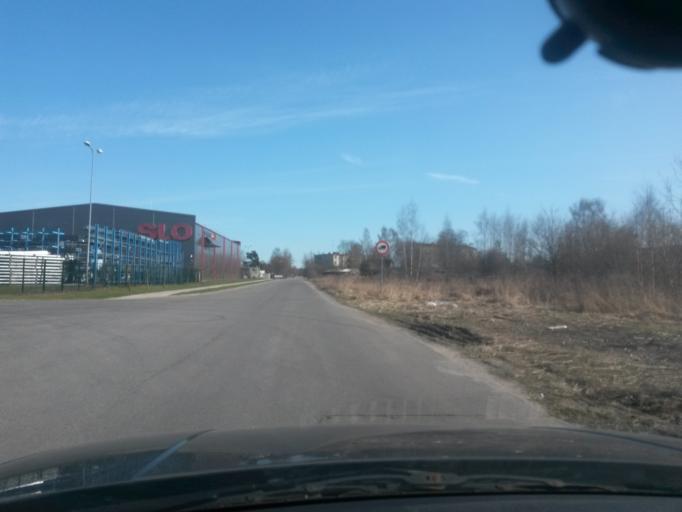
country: LV
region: Stopini
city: Ulbroka
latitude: 56.9089
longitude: 24.2178
